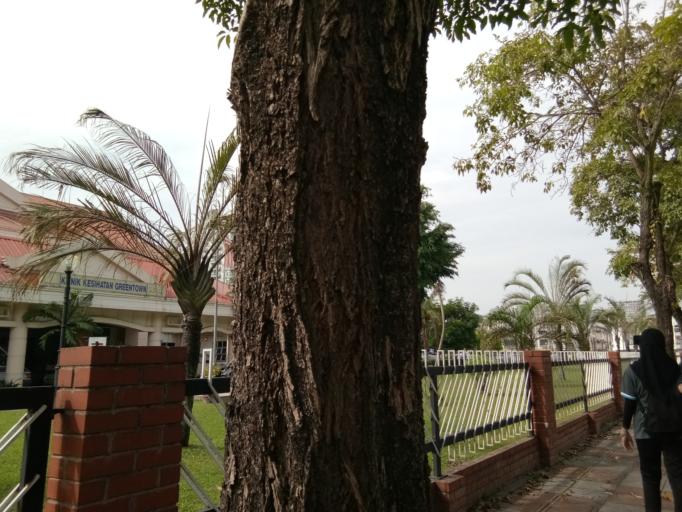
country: MY
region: Perak
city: Ipoh
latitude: 4.6030
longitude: 101.0869
